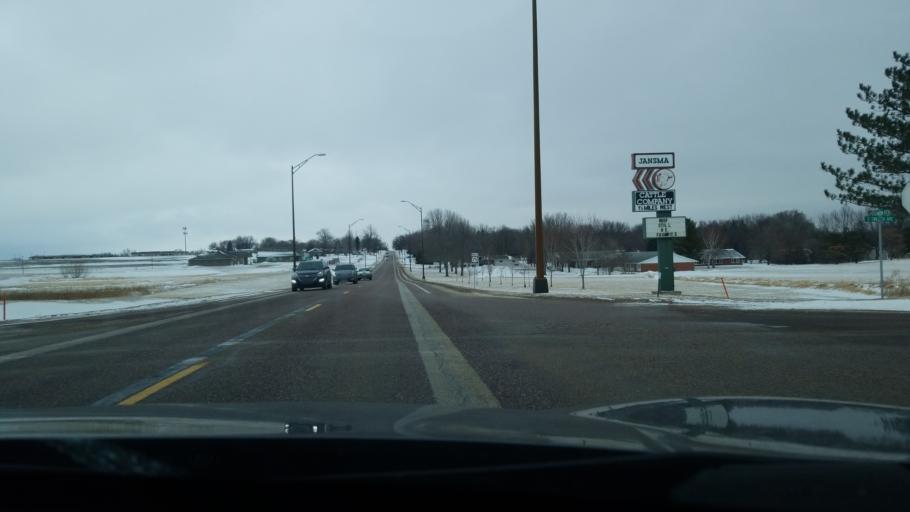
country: US
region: Iowa
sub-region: Lyon County
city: Rock Rapids
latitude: 43.4187
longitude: -96.1758
